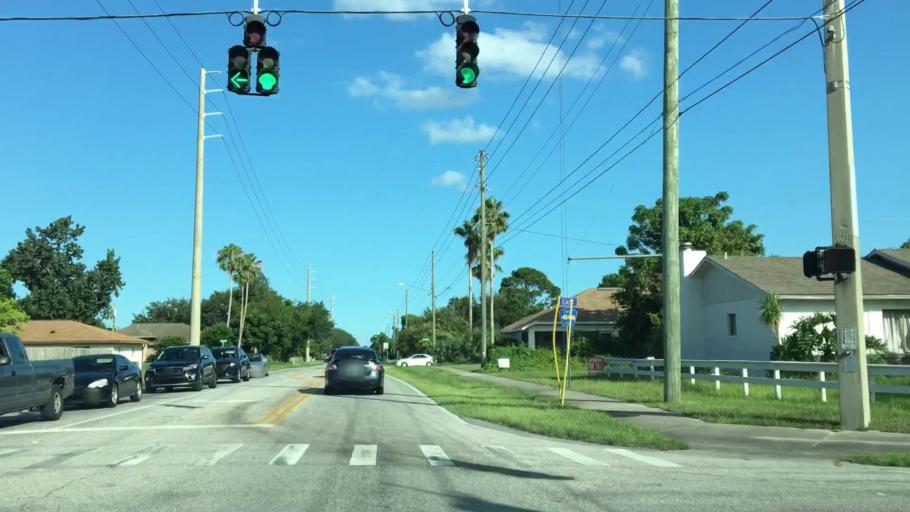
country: US
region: Florida
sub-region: Volusia County
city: Deltona
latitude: 28.9008
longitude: -81.2398
